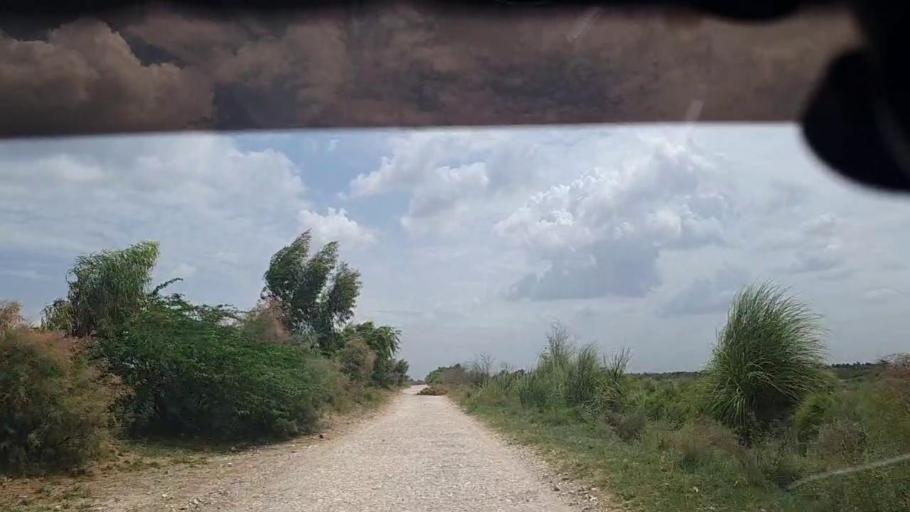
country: PK
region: Sindh
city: Rustam jo Goth
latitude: 28.0489
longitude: 68.9400
